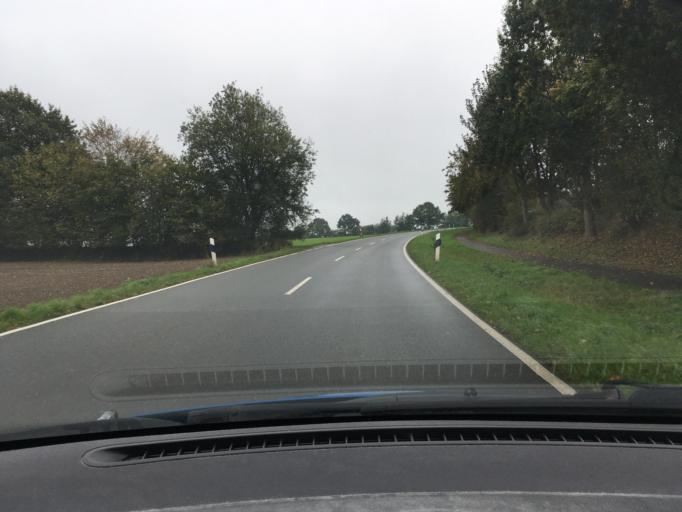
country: DE
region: Schleswig-Holstein
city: Bosdorf
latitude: 54.1100
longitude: 10.4796
